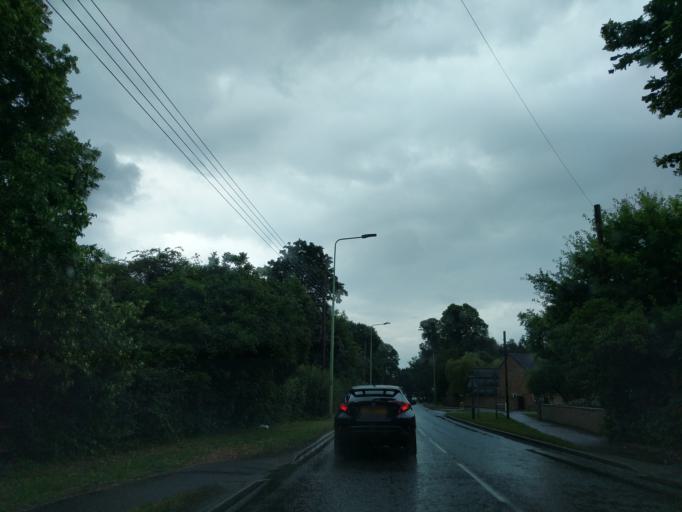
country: GB
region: England
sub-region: Suffolk
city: Lakenheath
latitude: 52.3445
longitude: 0.5226
